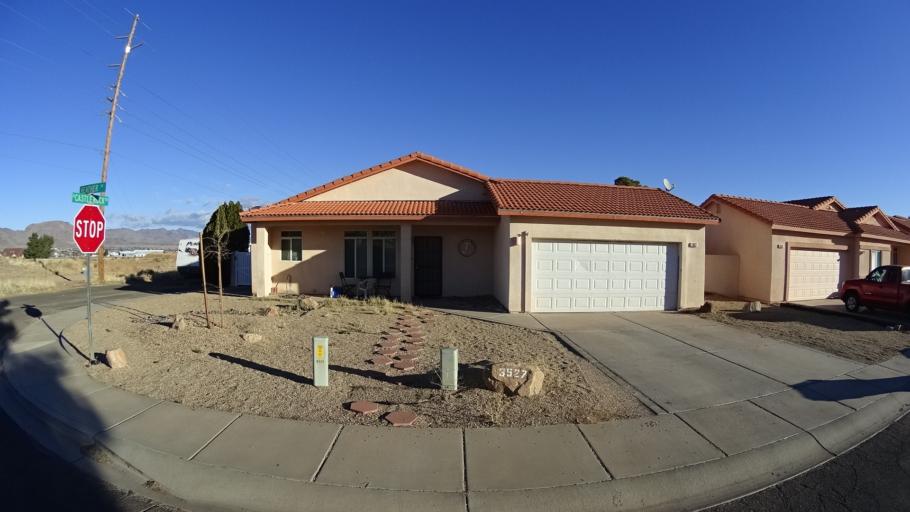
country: US
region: Arizona
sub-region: Mohave County
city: New Kingman-Butler
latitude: 35.2254
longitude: -113.9935
